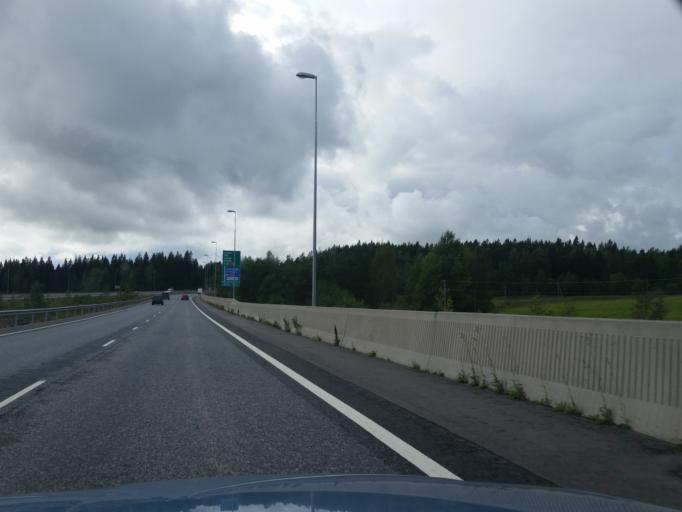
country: FI
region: Uusimaa
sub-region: Helsinki
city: Vihti
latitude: 60.3008
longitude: 24.2394
